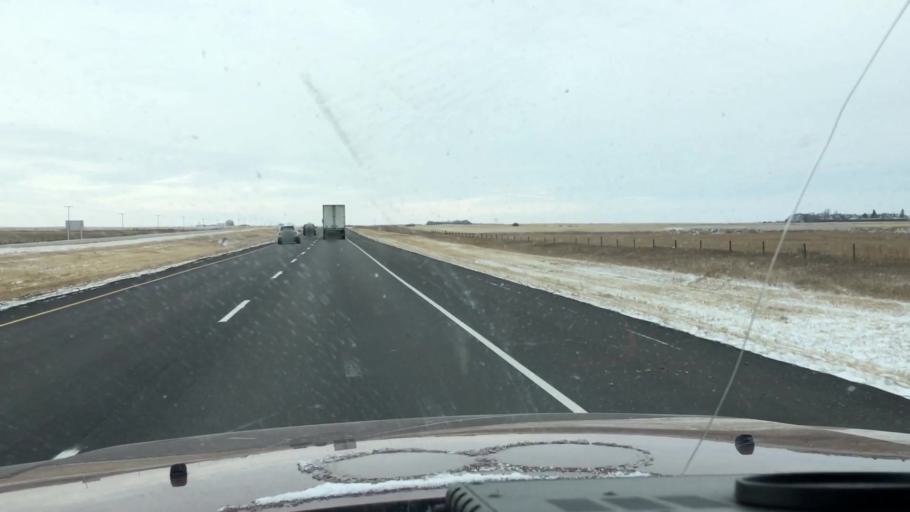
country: CA
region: Saskatchewan
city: Saskatoon
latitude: 51.8022
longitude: -106.4908
